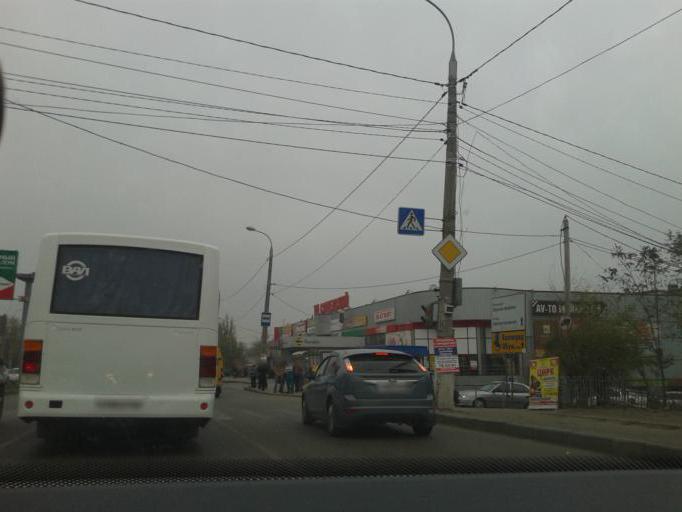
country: RU
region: Volgograd
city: Volgograd
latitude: 48.6487
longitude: 44.4346
